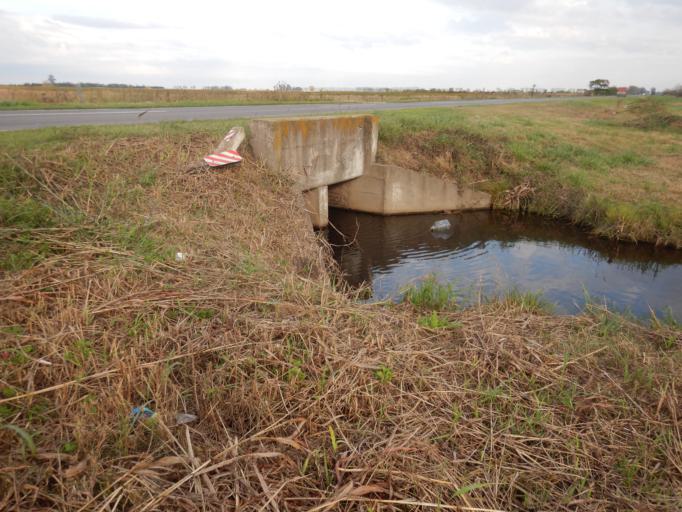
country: AR
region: Santa Fe
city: Roldan
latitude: -32.8995
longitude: -60.9420
